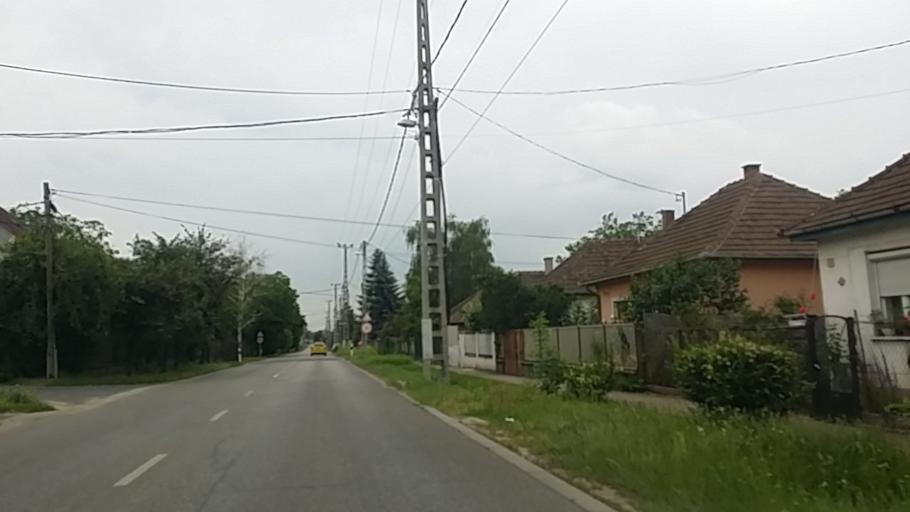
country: HU
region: Pest
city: Vecses
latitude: 47.4105
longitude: 19.2514
